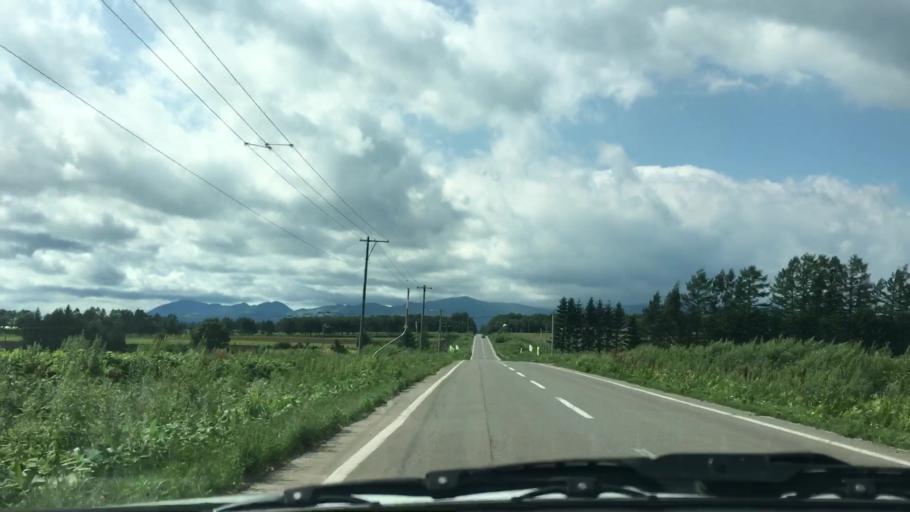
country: JP
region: Hokkaido
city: Otofuke
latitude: 43.2759
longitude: 143.3759
